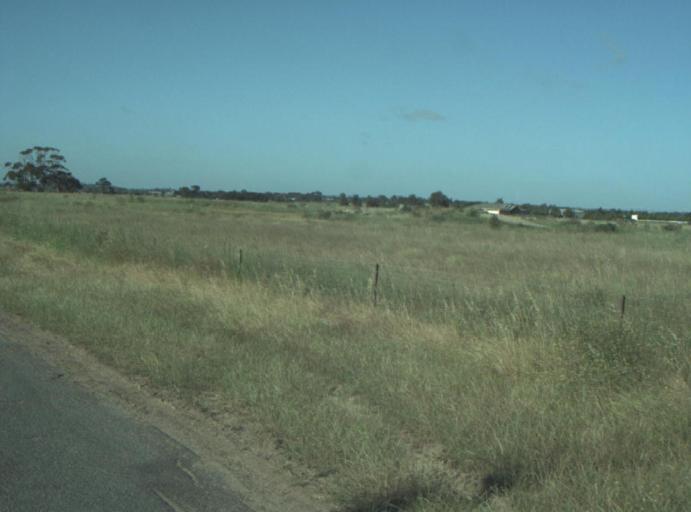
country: AU
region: Victoria
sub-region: Wyndham
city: Little River
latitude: -37.9843
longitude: 144.4593
